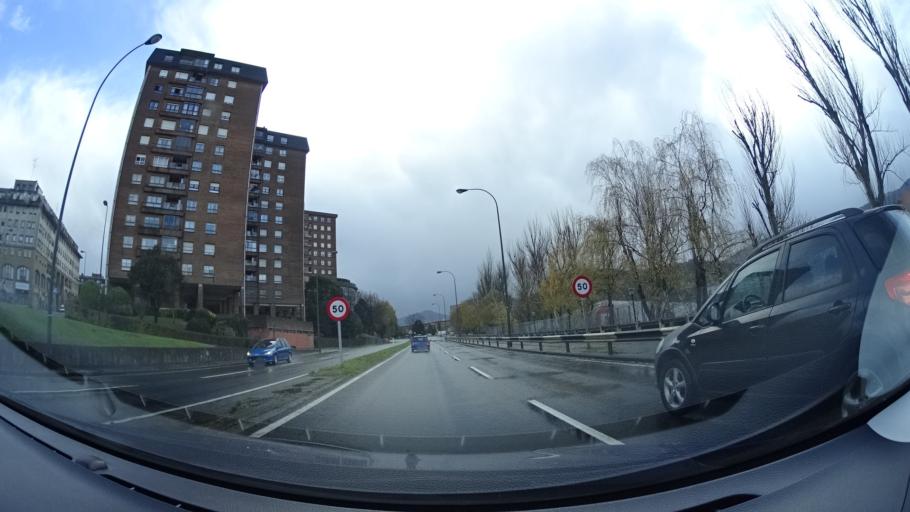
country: ES
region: Basque Country
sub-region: Bizkaia
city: Santutxu
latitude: 43.2512
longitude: -2.9069
